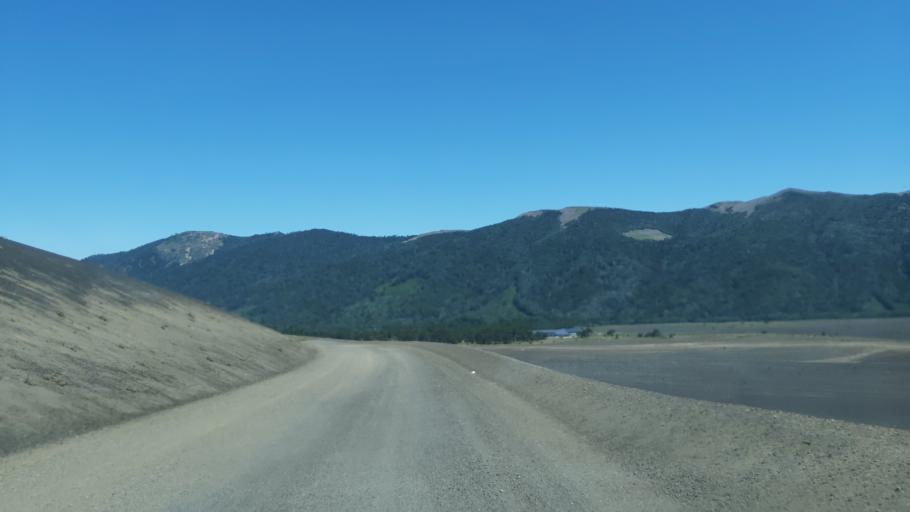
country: CL
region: Araucania
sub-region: Provincia de Cautin
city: Vilcun
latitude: -38.4095
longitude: -71.5424
